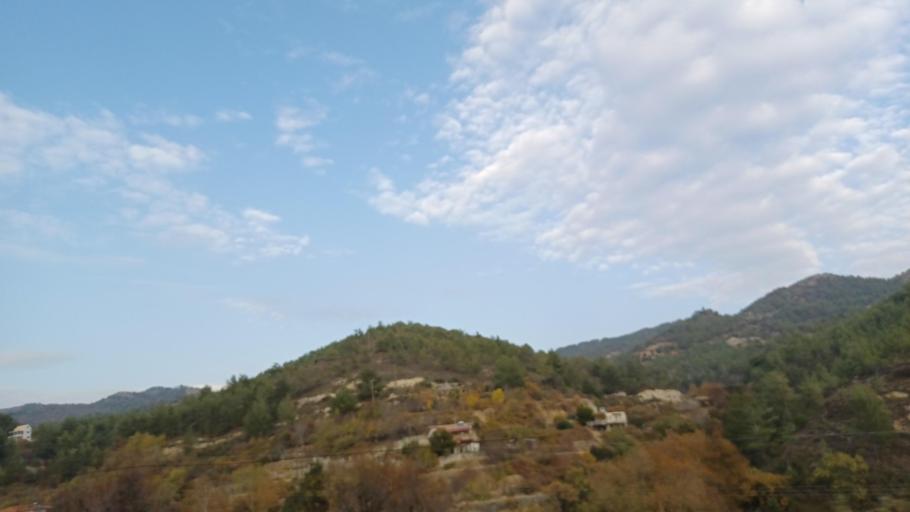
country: CY
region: Limassol
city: Pelendri
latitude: 34.9103
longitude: 32.9427
